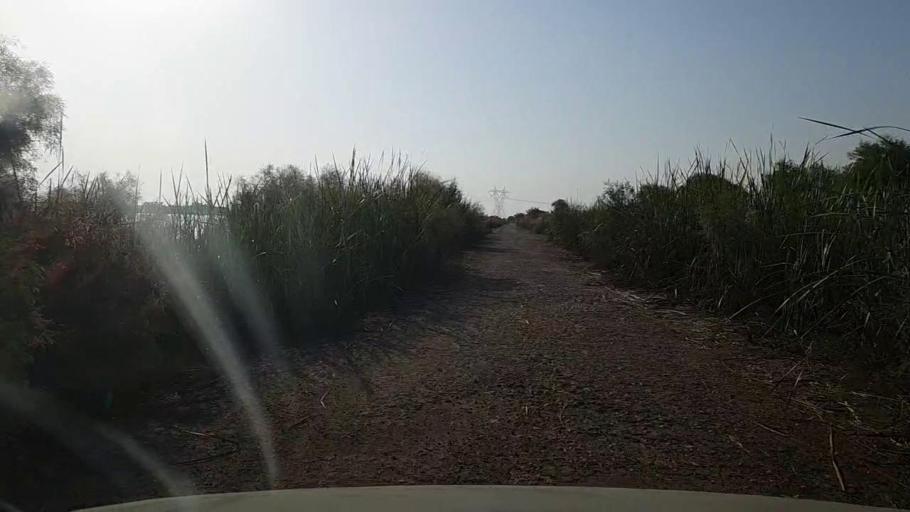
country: PK
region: Sindh
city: Kandhkot
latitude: 28.2901
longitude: 69.3257
